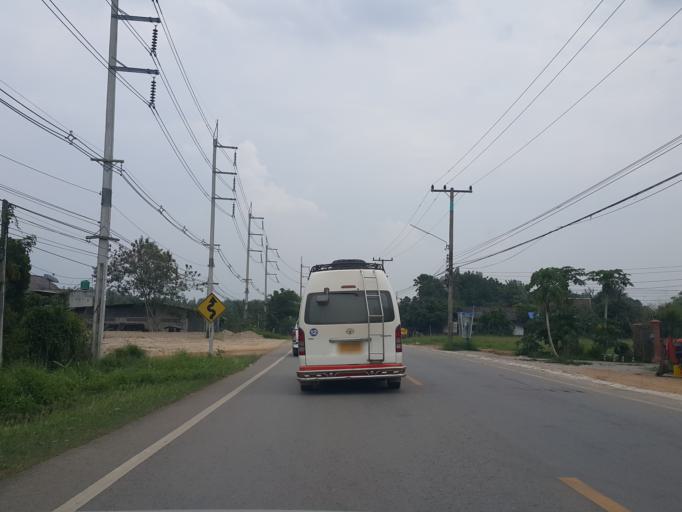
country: TH
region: Chiang Mai
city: Mae Taeng
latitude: 19.0906
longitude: 98.8872
